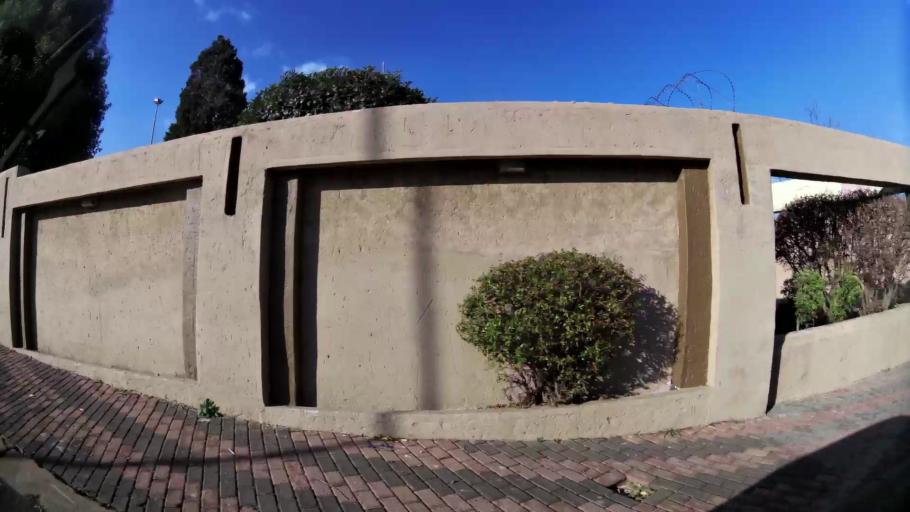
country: ZA
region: Gauteng
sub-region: City of Johannesburg Metropolitan Municipality
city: Soweto
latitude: -26.2750
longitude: 27.9146
